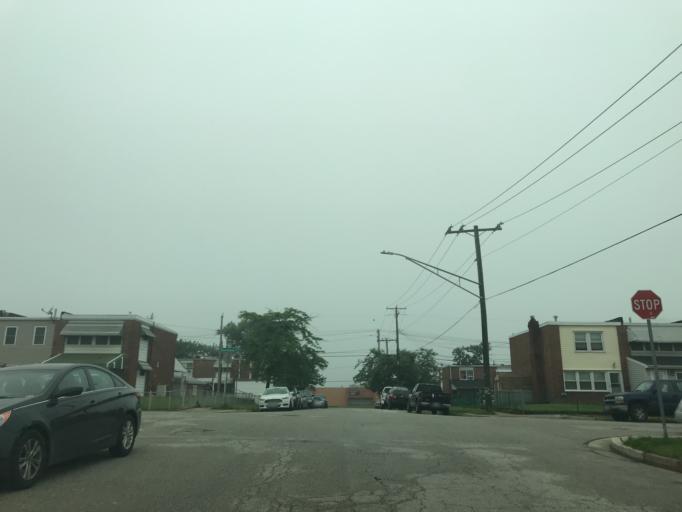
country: US
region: Maryland
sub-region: Baltimore County
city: Rosedale
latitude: 39.2984
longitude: -76.5135
